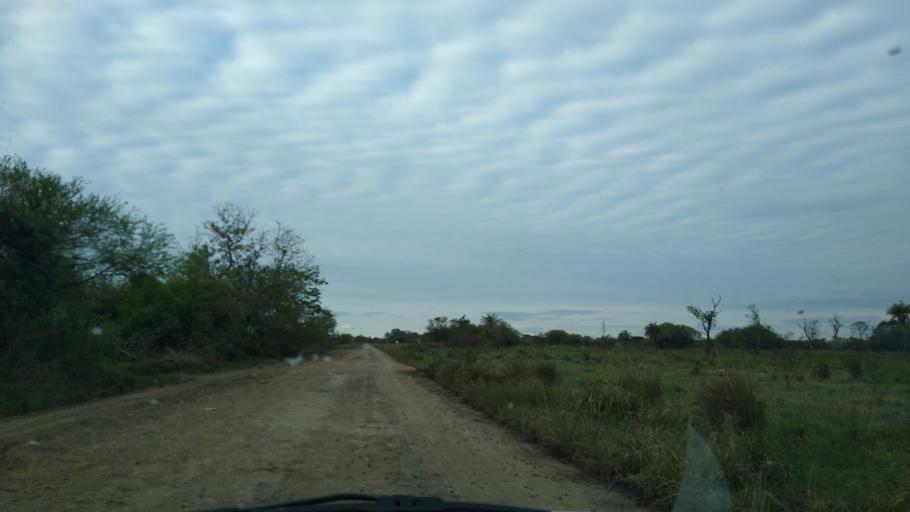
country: AR
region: Chaco
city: Puerto Tirol
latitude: -27.3906
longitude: -59.0499
